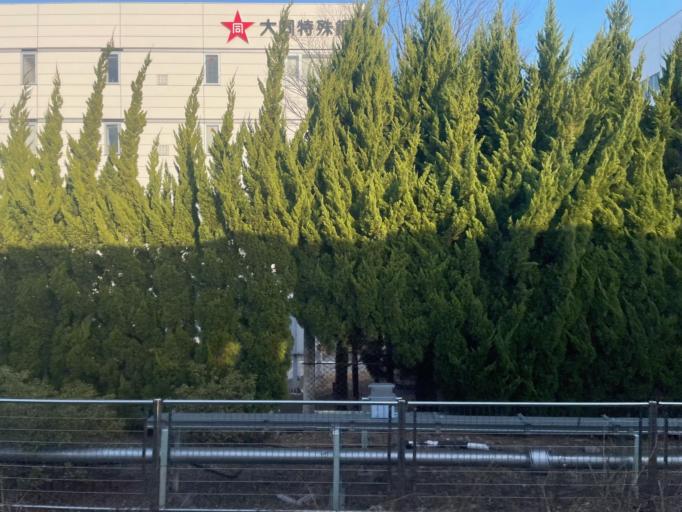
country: JP
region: Gunma
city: Shibukawa
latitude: 36.4881
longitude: 139.0077
